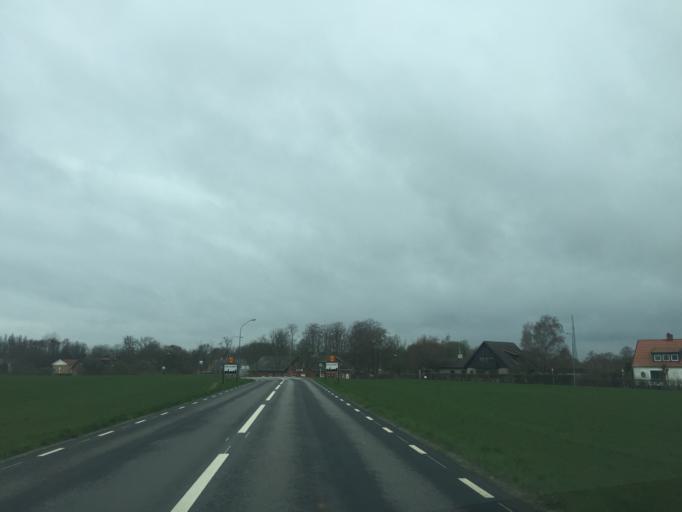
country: SE
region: Skane
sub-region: Skurups Kommun
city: Skivarp
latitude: 55.4257
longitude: 13.5866
